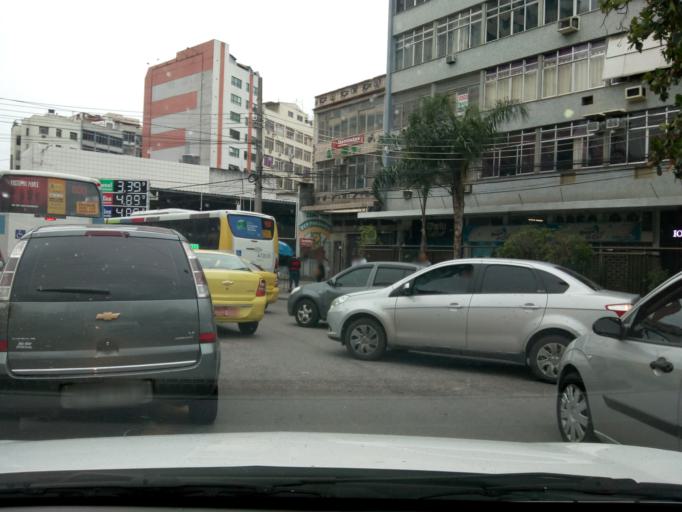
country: BR
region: Rio de Janeiro
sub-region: Rio De Janeiro
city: Rio de Janeiro
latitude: -22.9239
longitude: -43.2361
